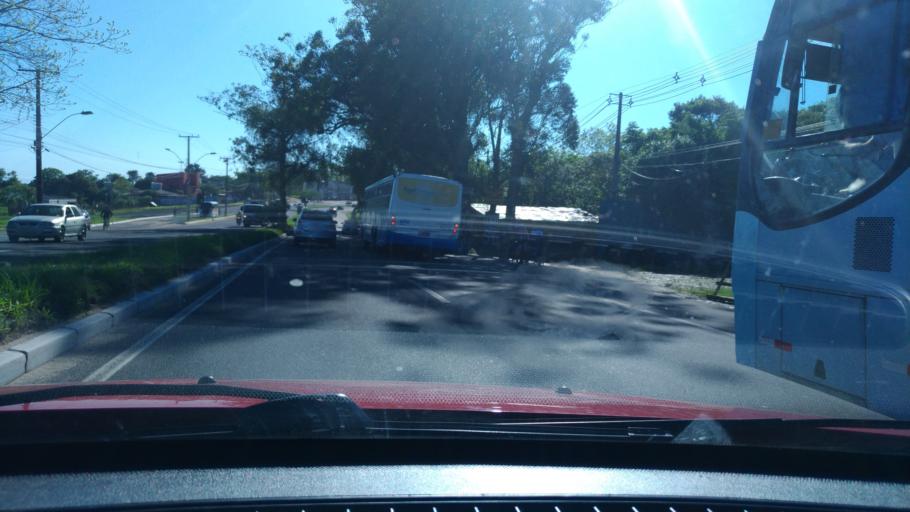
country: BR
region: Rio Grande do Sul
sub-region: Viamao
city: Viamao
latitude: -30.0942
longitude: -51.0783
